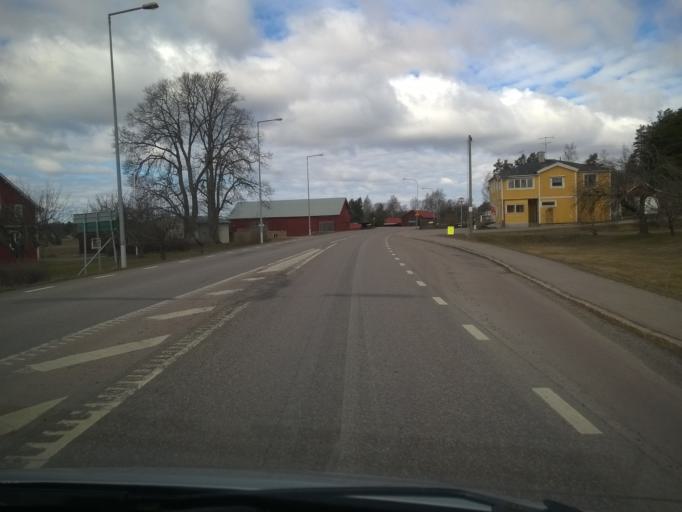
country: SE
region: Uppsala
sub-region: Tierps Kommun
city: Tierp
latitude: 60.2214
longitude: 17.4691
